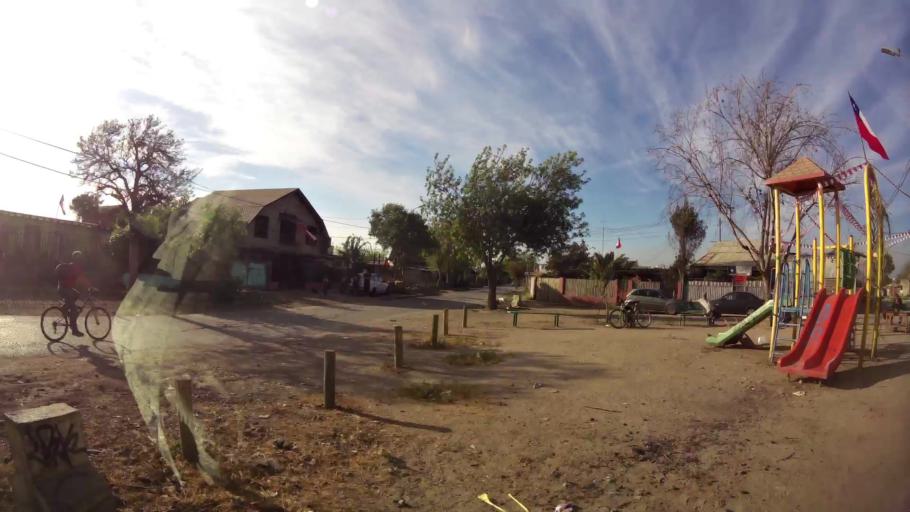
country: CL
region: Santiago Metropolitan
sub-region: Provincia de Santiago
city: Lo Prado
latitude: -33.4737
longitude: -70.6976
